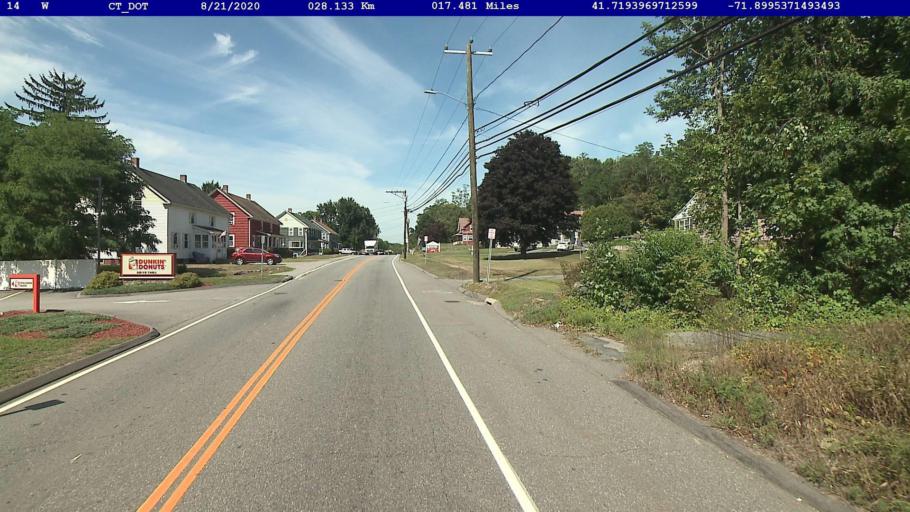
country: US
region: Connecticut
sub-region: Windham County
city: Moosup
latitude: 41.7195
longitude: -71.8995
